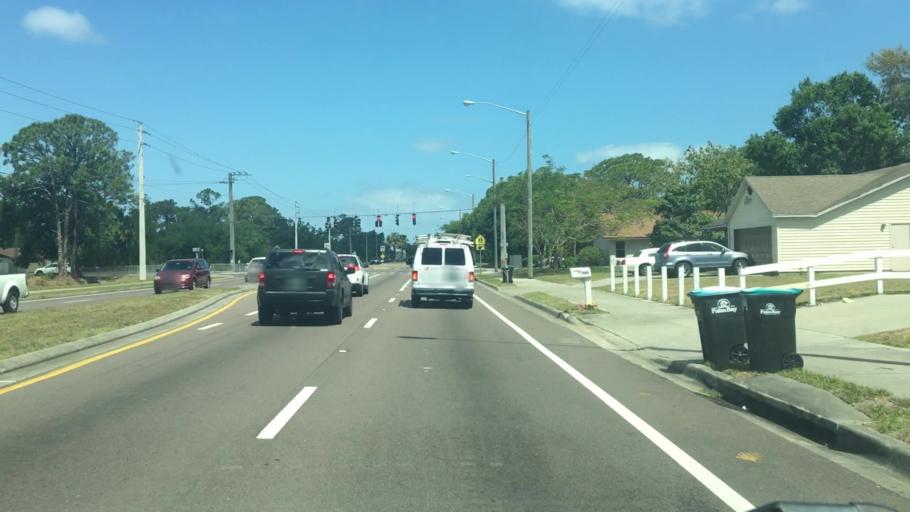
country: US
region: Florida
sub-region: Brevard County
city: Palm Bay
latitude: 28.0035
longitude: -80.6218
